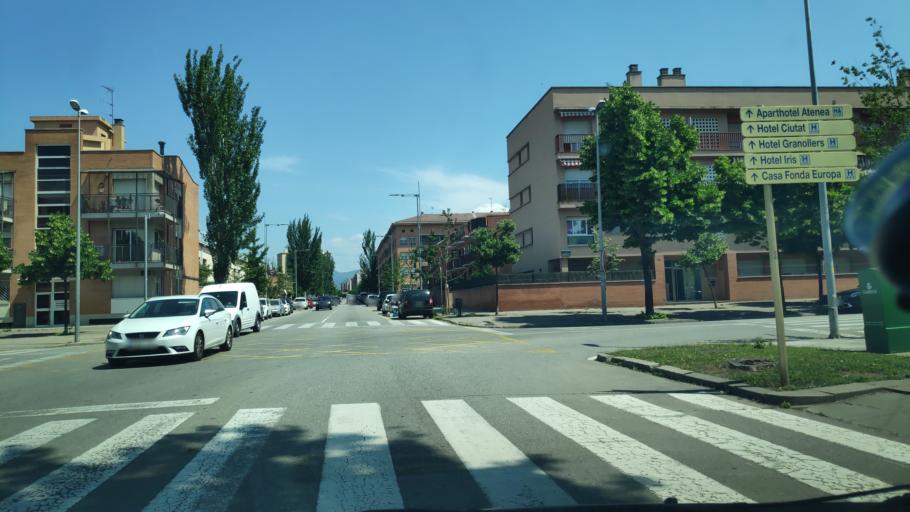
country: ES
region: Catalonia
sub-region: Provincia de Barcelona
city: Granollers
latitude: 41.5981
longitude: 2.2823
